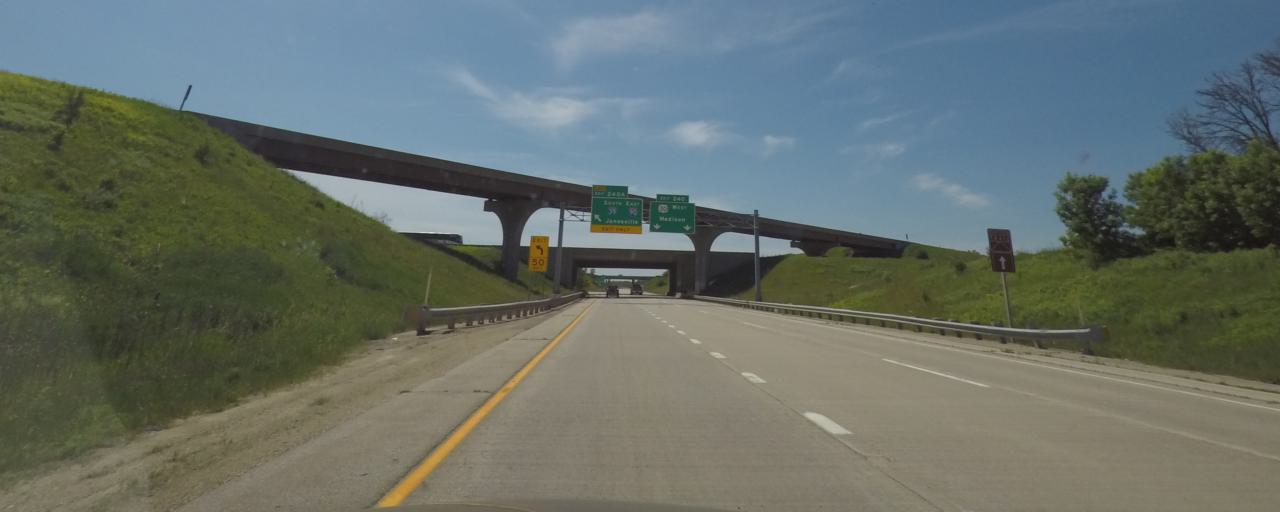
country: US
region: Wisconsin
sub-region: Dane County
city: Monona
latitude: 43.1040
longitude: -89.2797
